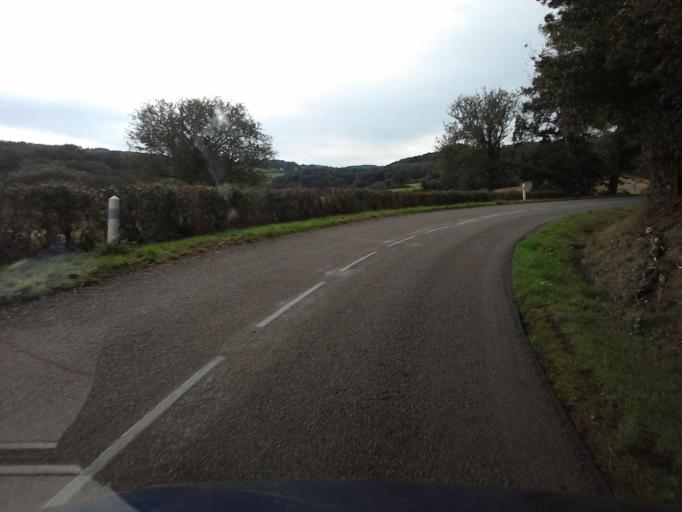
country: FR
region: Bourgogne
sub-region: Departement de la Nievre
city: Lormes
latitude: 47.2213
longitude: 3.8375
